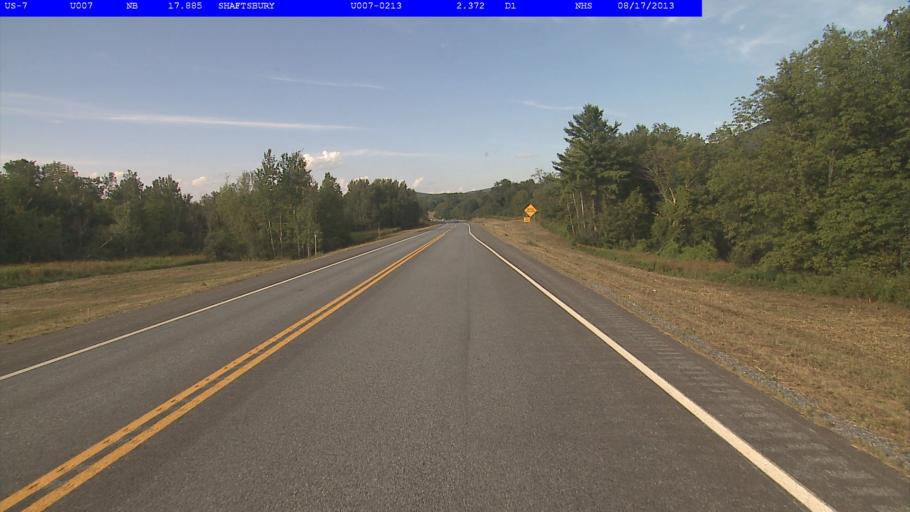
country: US
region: Vermont
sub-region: Bennington County
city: North Bennington
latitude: 42.9624
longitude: -73.1662
